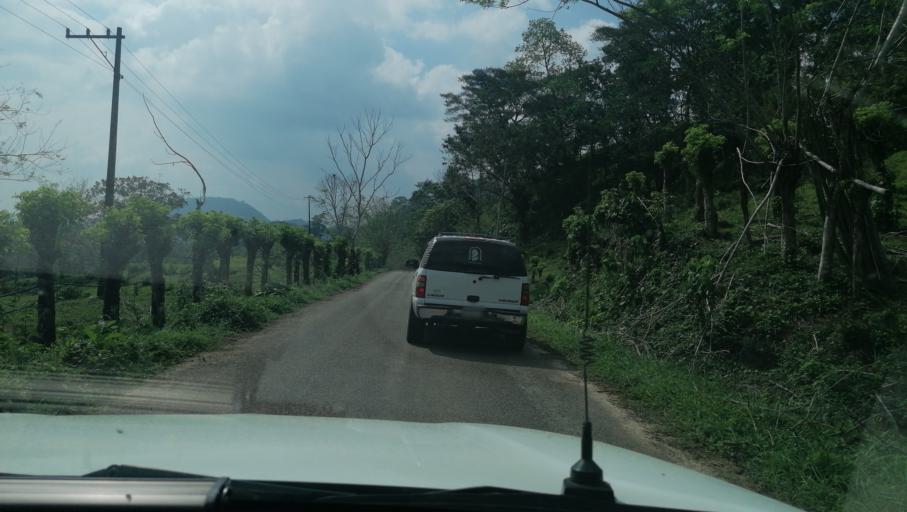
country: MX
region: Chiapas
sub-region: Francisco Leon
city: San Miguel la Sardina
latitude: 17.2340
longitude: -93.3357
